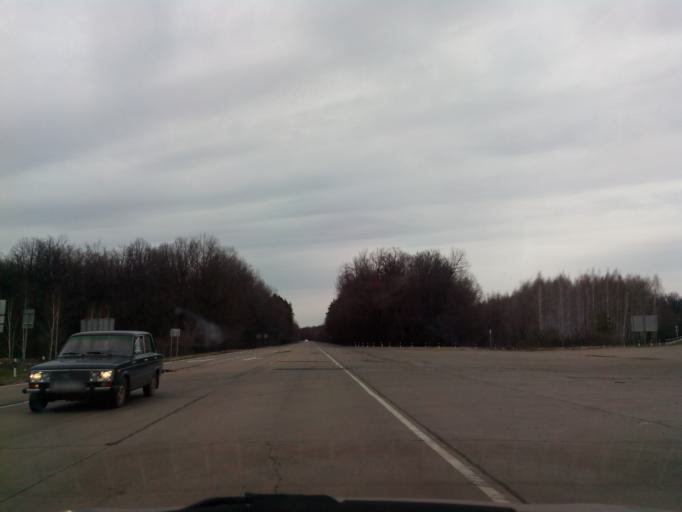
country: RU
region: Tambov
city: Bokino
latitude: 52.5597
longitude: 41.3551
